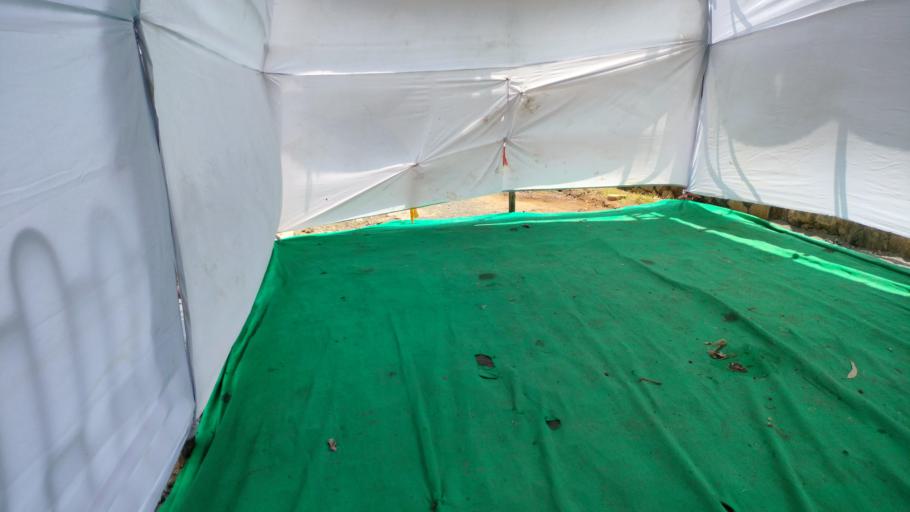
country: IN
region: Maharashtra
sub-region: Thane
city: Virar
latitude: 19.4768
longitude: 72.8257
